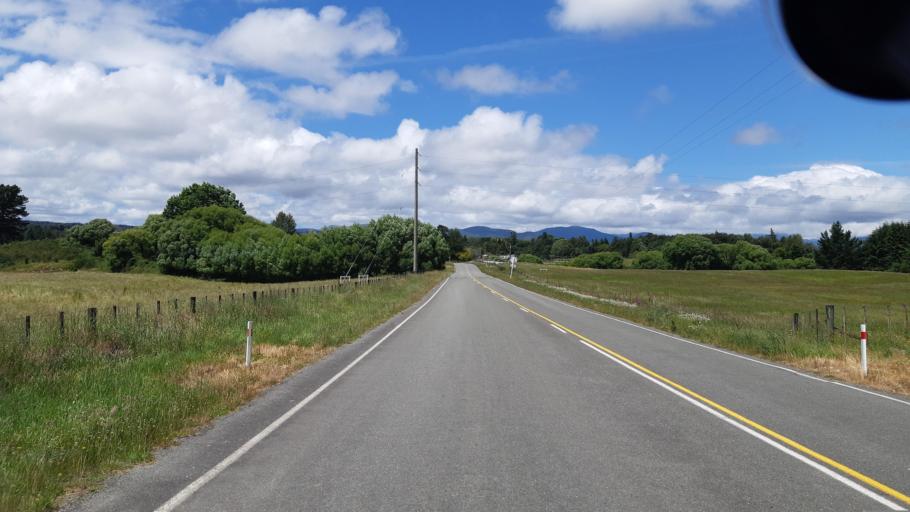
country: NZ
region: West Coast
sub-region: Grey District
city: Greymouth
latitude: -42.2720
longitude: 171.6765
